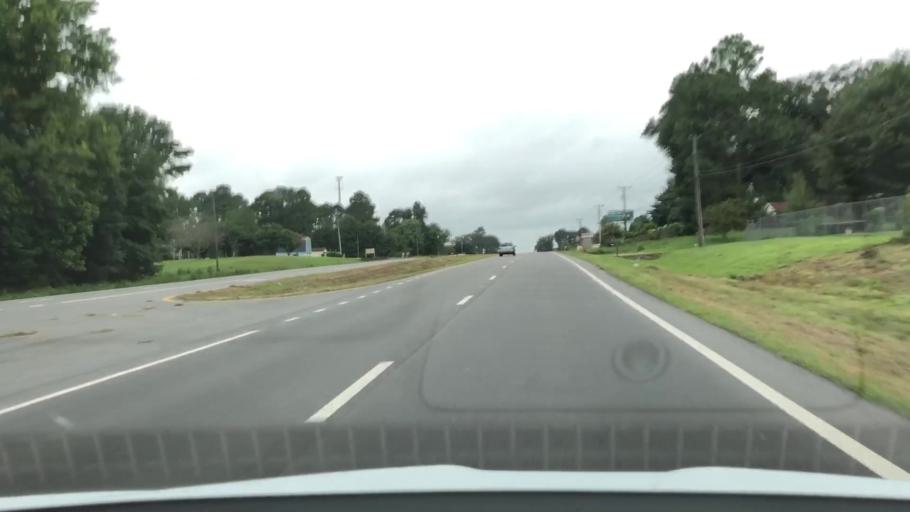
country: US
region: North Carolina
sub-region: Lenoir County
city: La Grange
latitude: 35.2757
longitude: -77.7457
